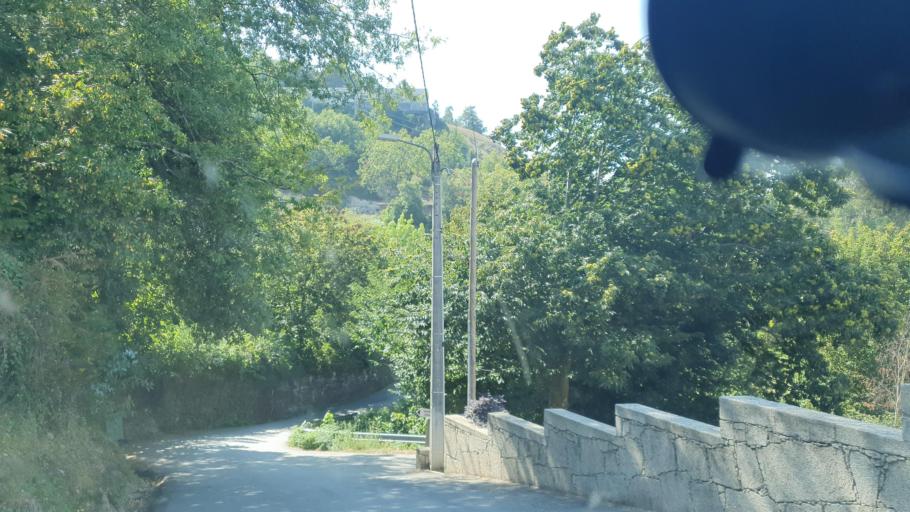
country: PT
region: Braga
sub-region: Vieira do Minho
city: Real
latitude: 41.6727
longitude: -8.1562
